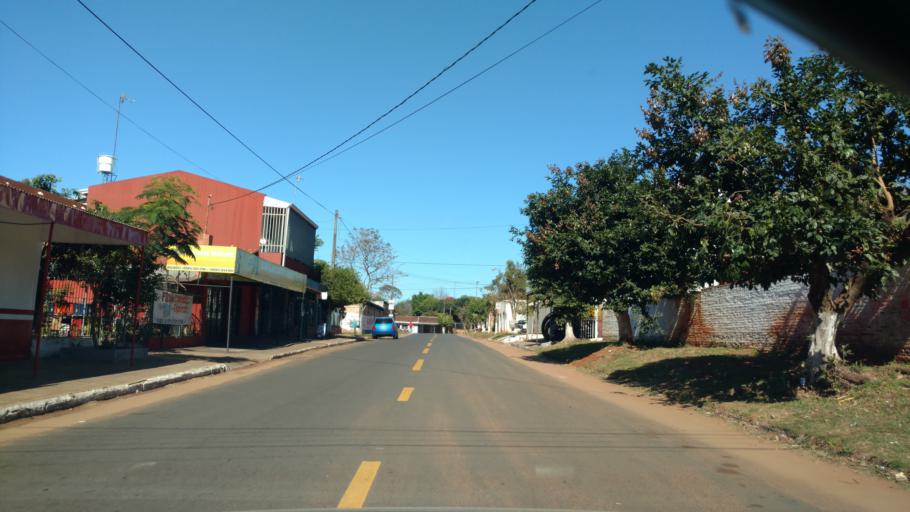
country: PY
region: Central
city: Capiata
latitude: -25.3728
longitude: -57.4073
